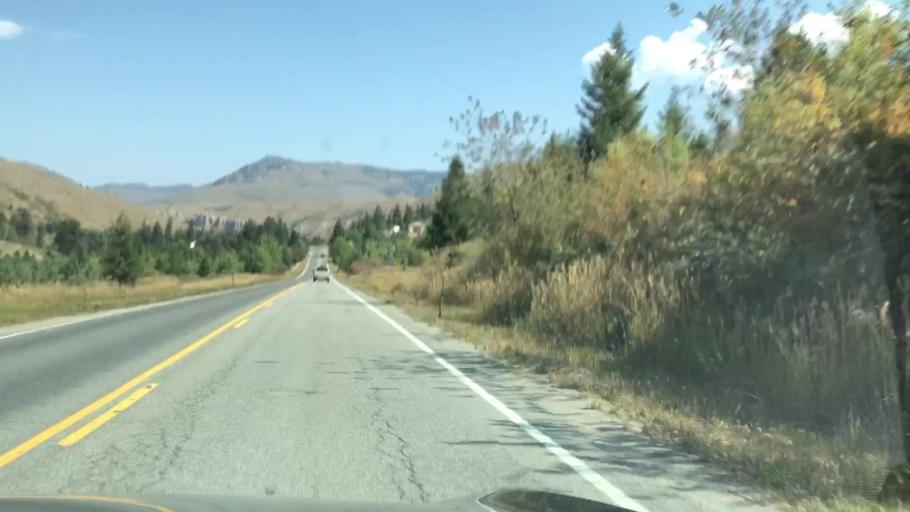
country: US
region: Wyoming
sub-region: Teton County
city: Hoback
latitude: 43.3335
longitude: -110.7266
